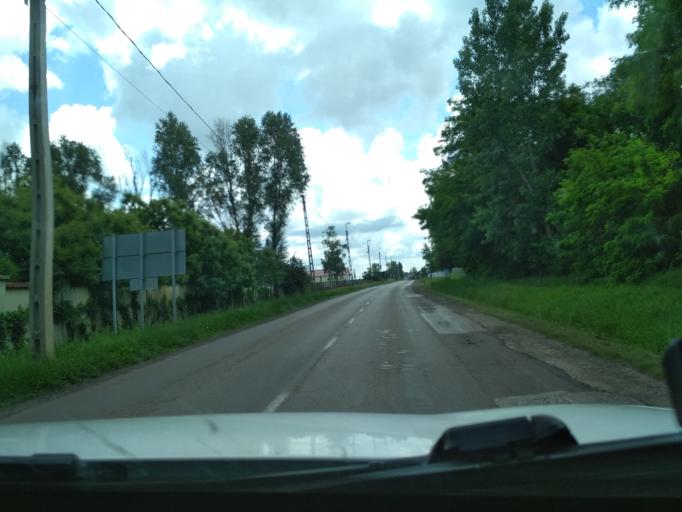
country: HU
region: Jasz-Nagykun-Szolnok
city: Tiszafured
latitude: 47.6045
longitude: 20.7636
